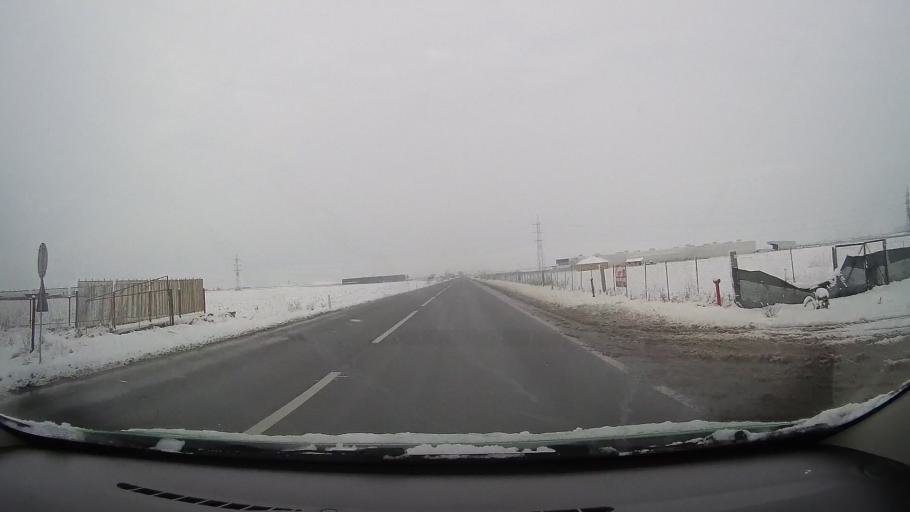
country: RO
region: Alba
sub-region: Municipiul Sebes
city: Lancram
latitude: 45.9619
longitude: 23.5348
